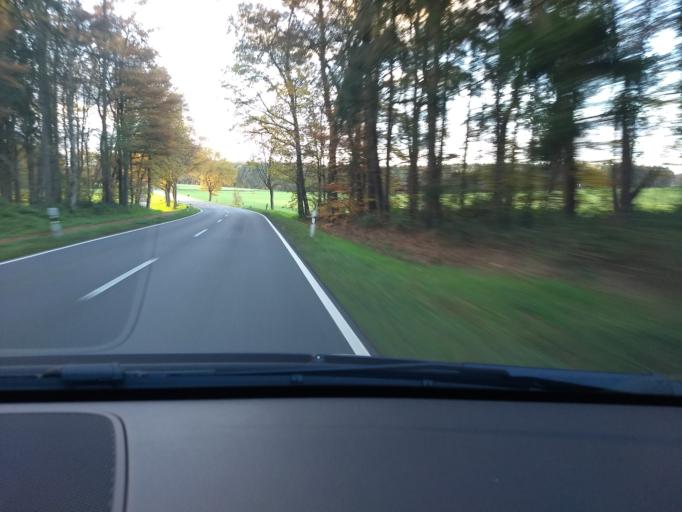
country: DE
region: North Rhine-Westphalia
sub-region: Regierungsbezirk Munster
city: Klein Reken
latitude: 51.7426
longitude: 7.0666
